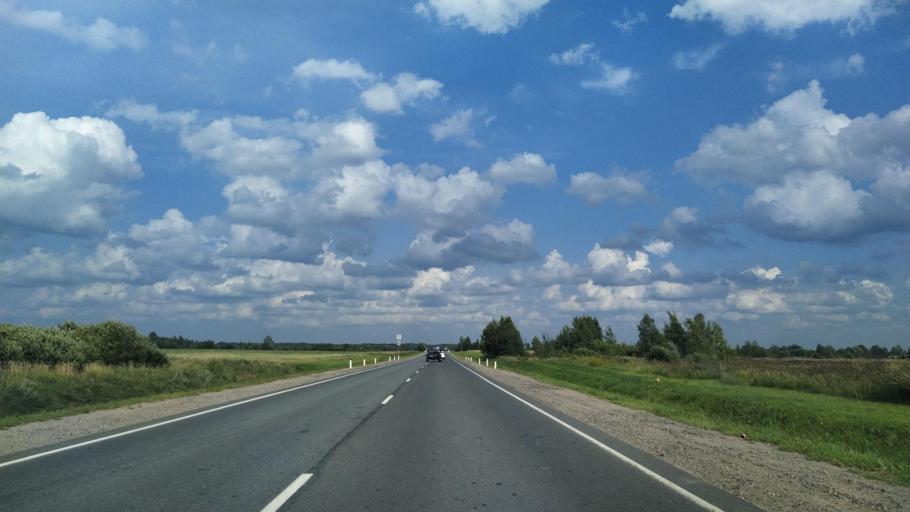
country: RU
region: Novgorod
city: Sol'tsy
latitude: 58.1324
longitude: 30.3726
